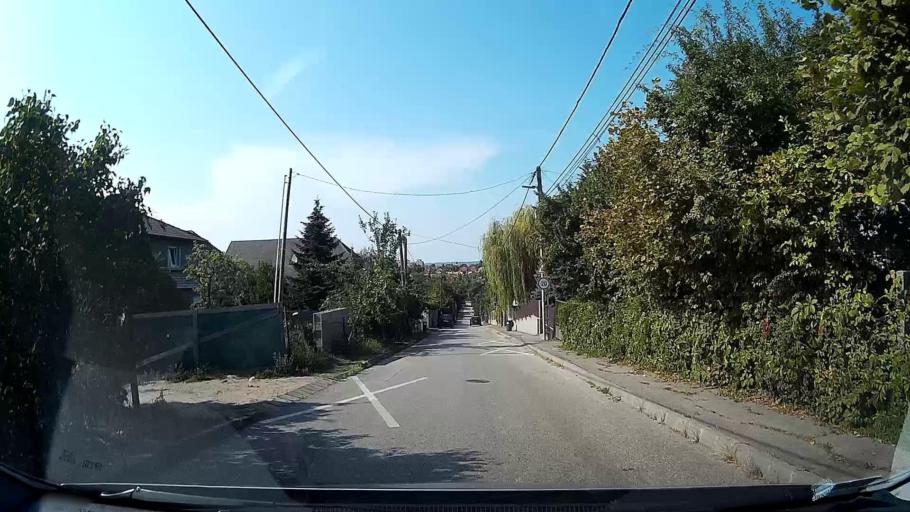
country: HU
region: Pest
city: Szentendre
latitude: 47.6813
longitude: 19.0743
